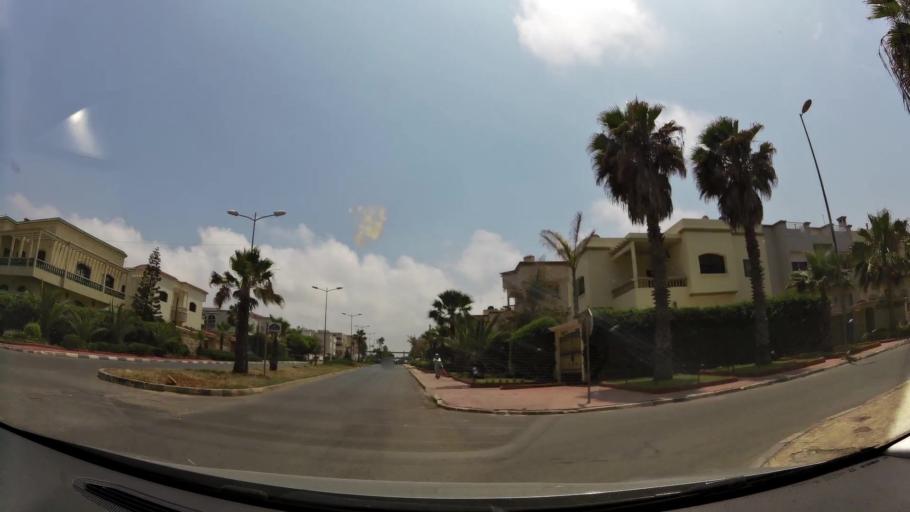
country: MA
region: Rabat-Sale-Zemmour-Zaer
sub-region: Skhirate-Temara
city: Temara
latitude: 33.9692
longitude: -6.9055
